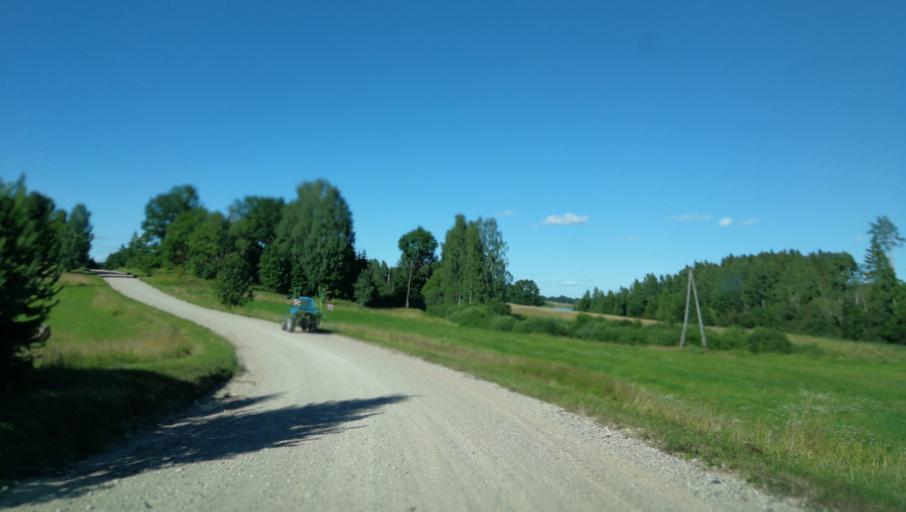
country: LV
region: Jaunpiebalga
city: Jaunpiebalga
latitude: 56.9981
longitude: 26.0290
